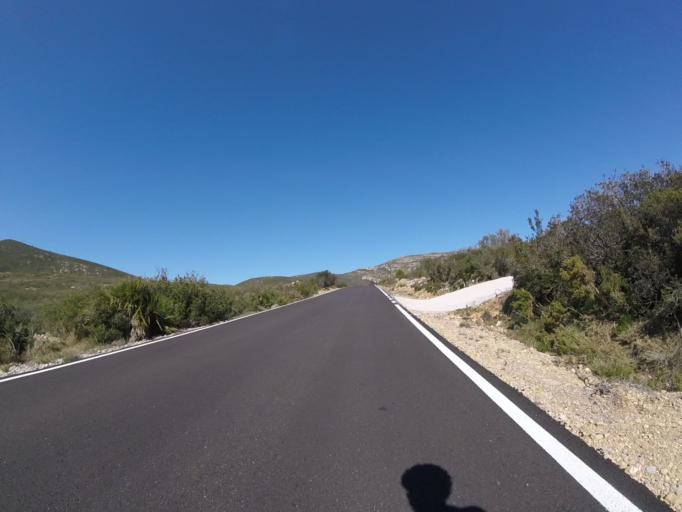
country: ES
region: Valencia
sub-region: Provincia de Castello
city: Cervera del Maestre
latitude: 40.4016
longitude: 0.2311
